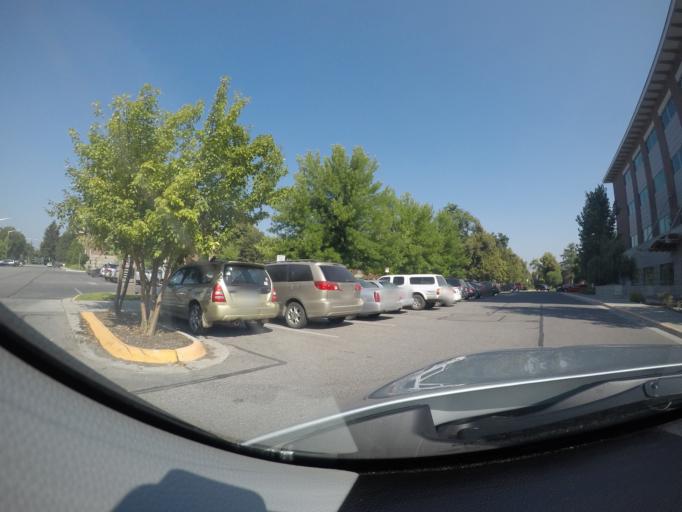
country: US
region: Montana
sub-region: Missoula County
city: Missoula
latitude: 46.8577
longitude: -113.9869
